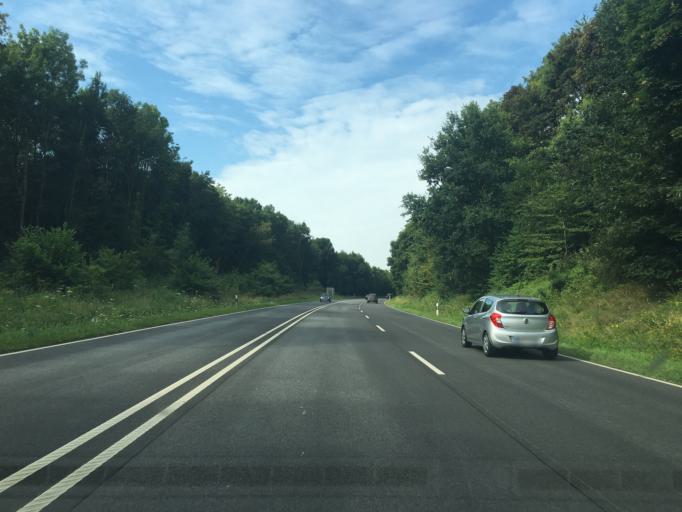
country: DE
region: Rheinland-Pfalz
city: Holler
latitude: 50.4260
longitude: 7.8285
